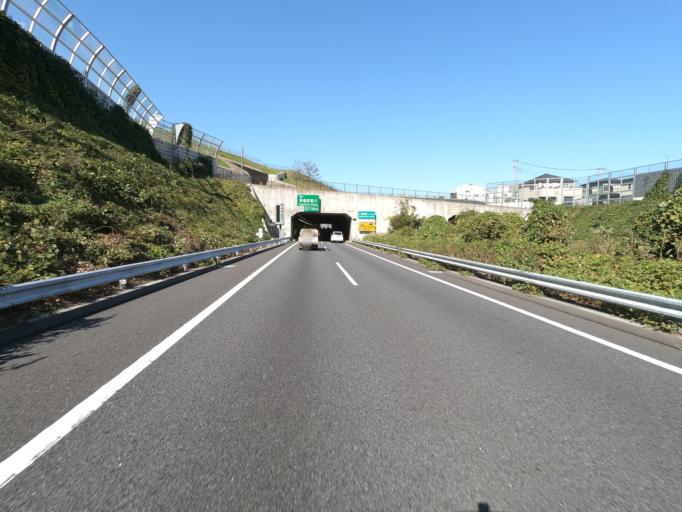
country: JP
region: Kanagawa
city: Zama
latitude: 35.5153
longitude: 139.3601
